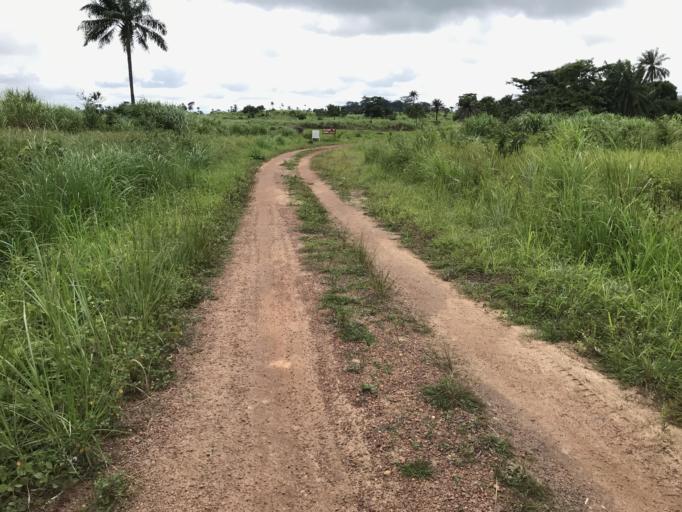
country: GN
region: Nzerekore
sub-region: Prefecture de Guekedou
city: Gueckedou
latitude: 8.4717
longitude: -10.2778
